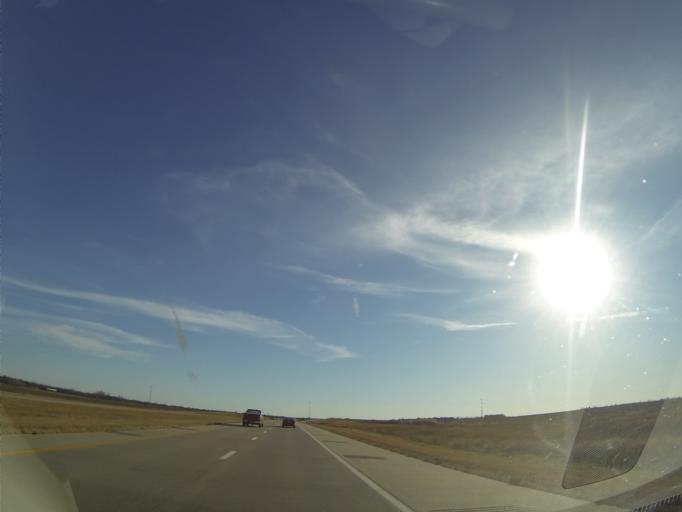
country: US
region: Kansas
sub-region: McPherson County
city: Lindsborg
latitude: 38.6900
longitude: -97.6219
